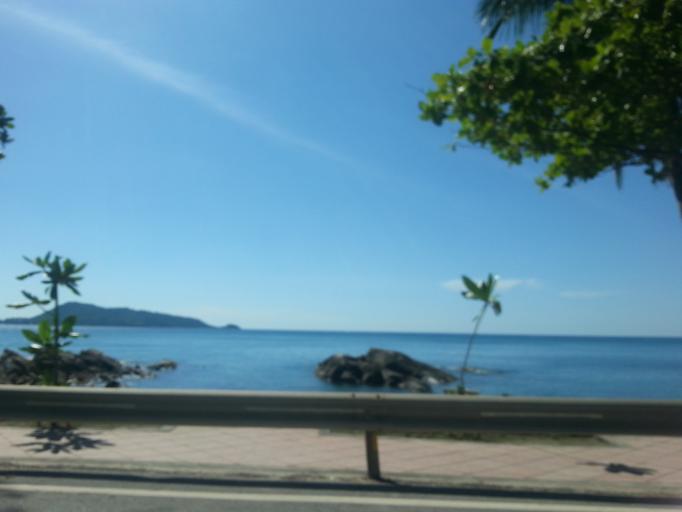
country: TH
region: Phuket
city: Patong
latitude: 7.9090
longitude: 98.2967
